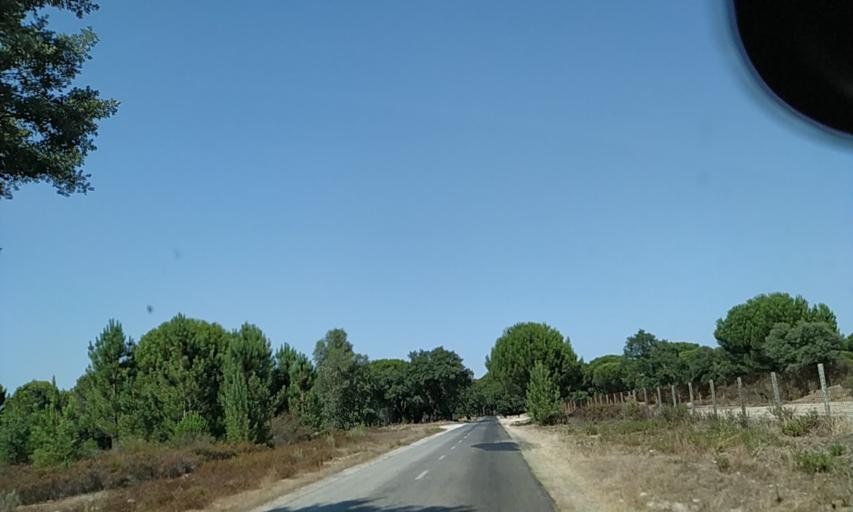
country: PT
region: Santarem
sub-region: Benavente
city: Poceirao
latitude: 38.7331
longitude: -8.7003
